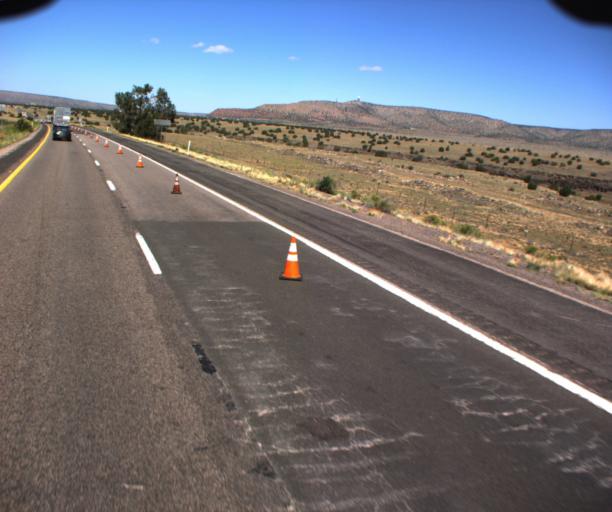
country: US
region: Arizona
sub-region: Mohave County
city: Peach Springs
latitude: 35.3216
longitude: -112.8995
